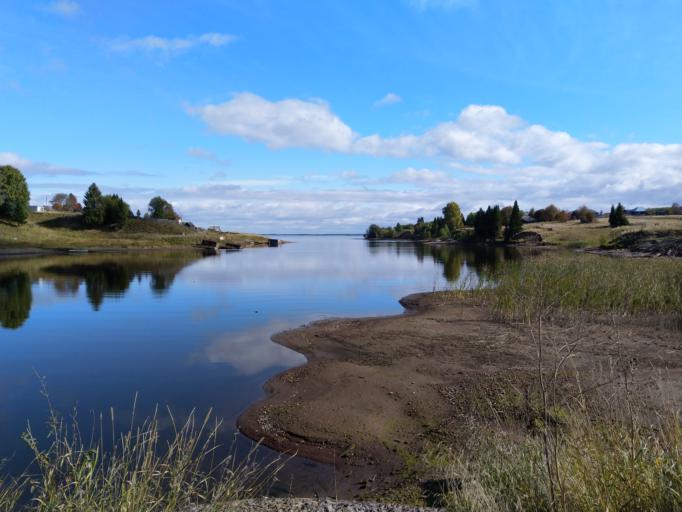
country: RU
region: Perm
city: Pozhva
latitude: 59.1454
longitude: 56.1835
